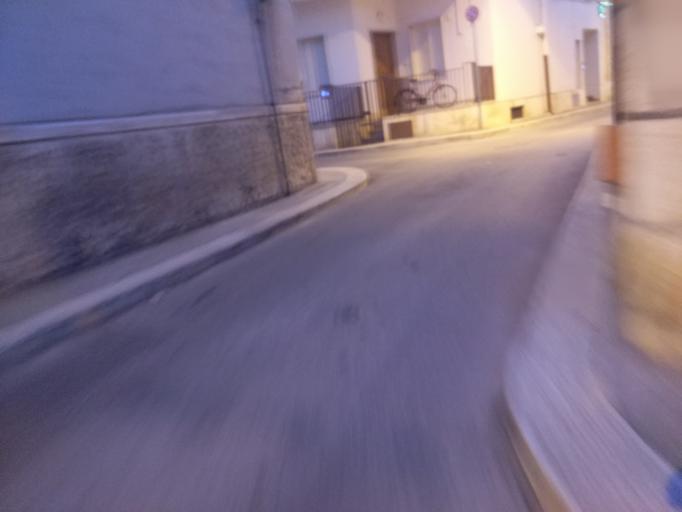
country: IT
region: Apulia
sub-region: Provincia di Bari
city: Modugno
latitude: 41.0803
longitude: 16.7797
